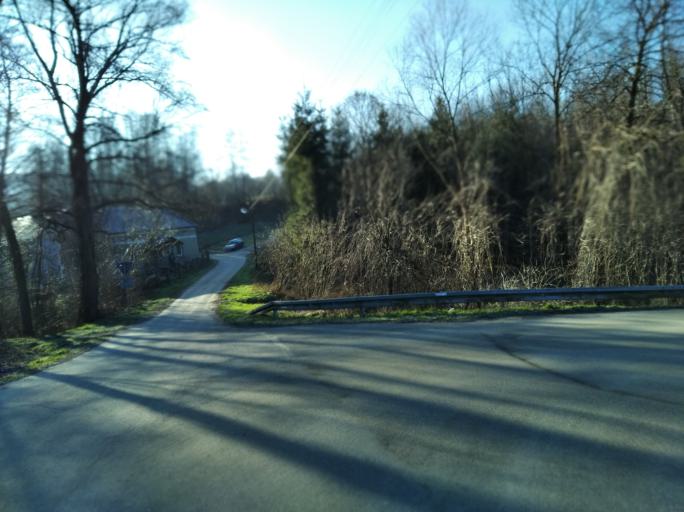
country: PL
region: Subcarpathian Voivodeship
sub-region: Powiat strzyzowski
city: Wysoka Strzyzowska
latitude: 49.8415
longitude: 21.7715
